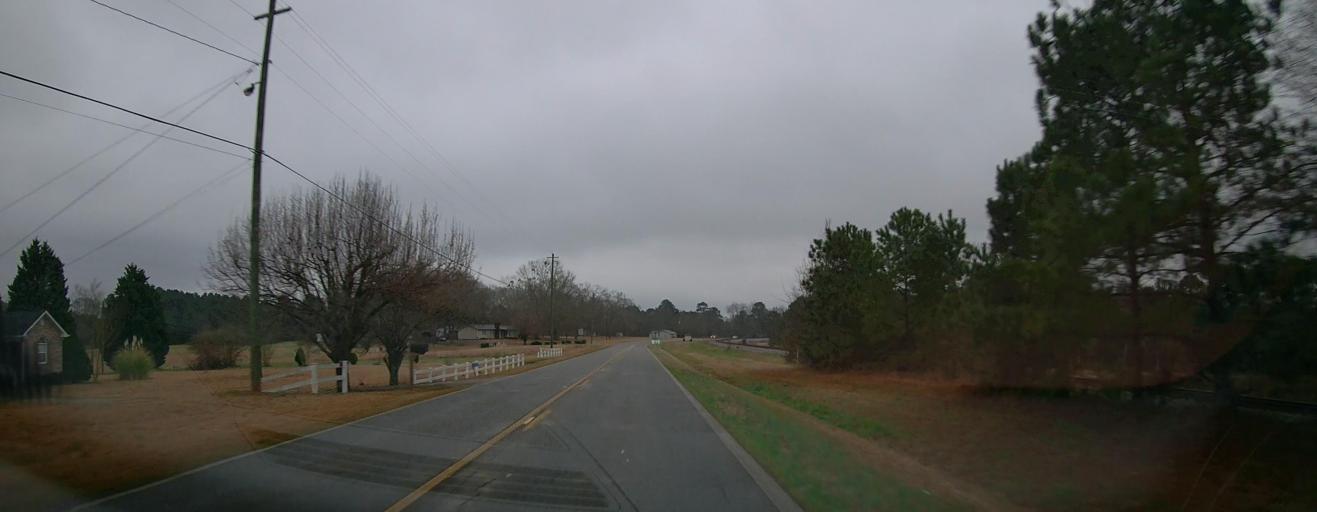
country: US
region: Georgia
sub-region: Lamar County
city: Barnesville
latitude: 33.1338
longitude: -84.1927
